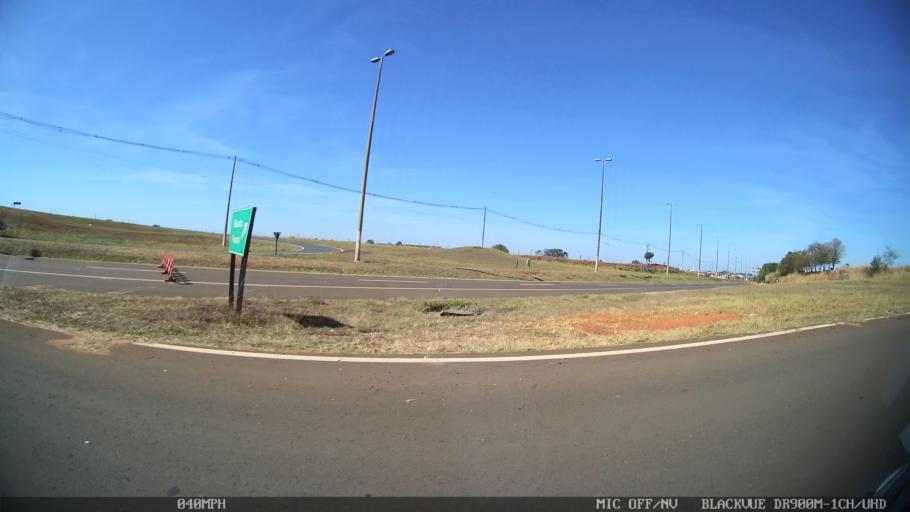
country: BR
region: Sao Paulo
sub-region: Barretos
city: Barretos
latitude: -20.5283
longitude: -48.5903
